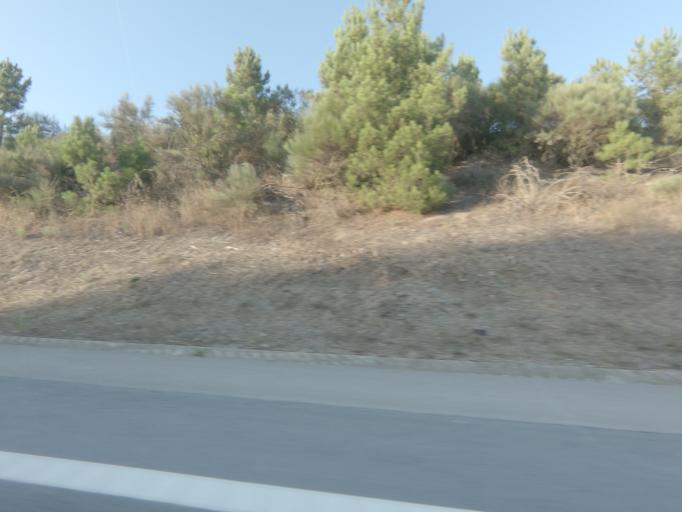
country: PT
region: Vila Real
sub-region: Vila Real
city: Vila Real
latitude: 41.3123
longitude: -7.6880
